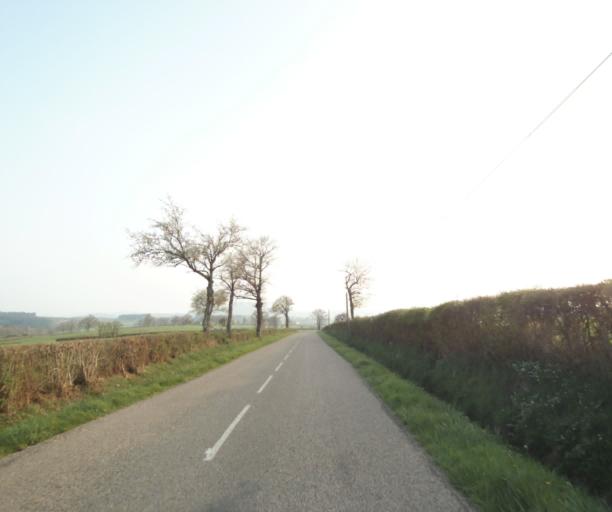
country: FR
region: Bourgogne
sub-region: Departement de Saone-et-Loire
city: Charolles
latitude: 46.4481
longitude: 4.4282
